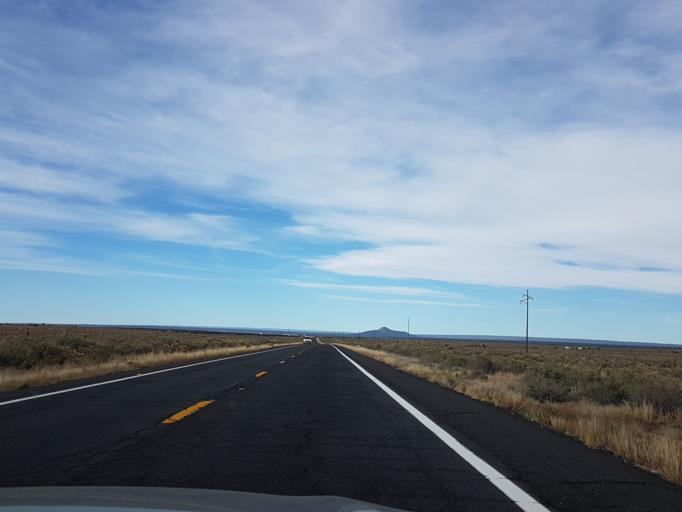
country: US
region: Arizona
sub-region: Coconino County
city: Williams
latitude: 35.6105
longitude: -112.1452
